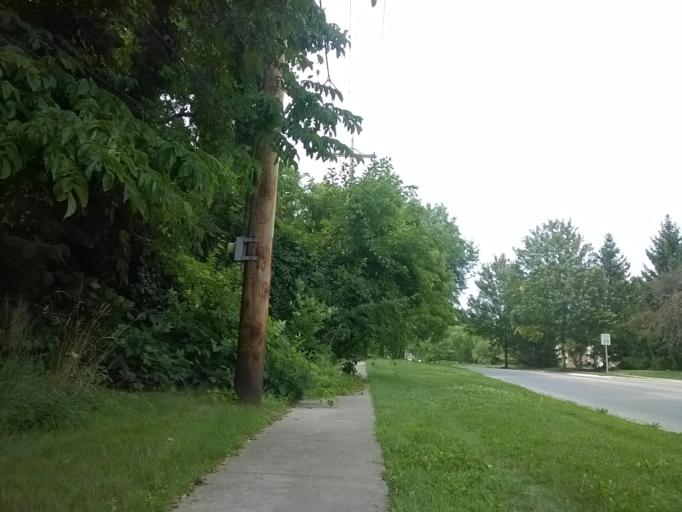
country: US
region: Indiana
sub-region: Hamilton County
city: Carmel
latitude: 39.9686
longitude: -86.1411
